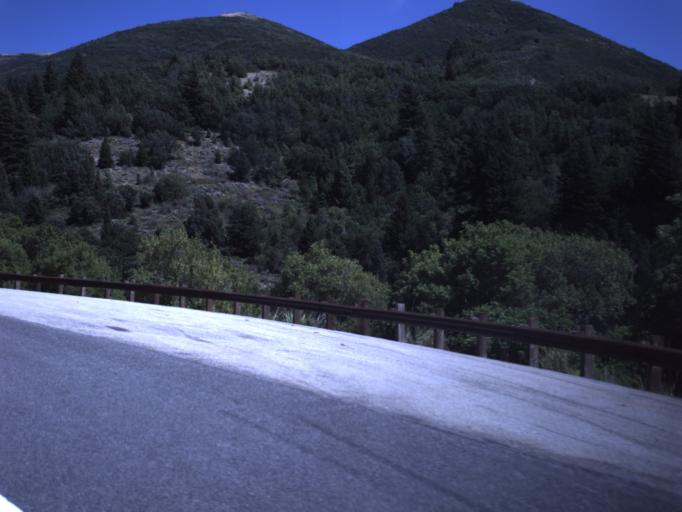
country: US
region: Utah
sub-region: Wasatch County
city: Midway
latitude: 40.3797
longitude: -111.5523
